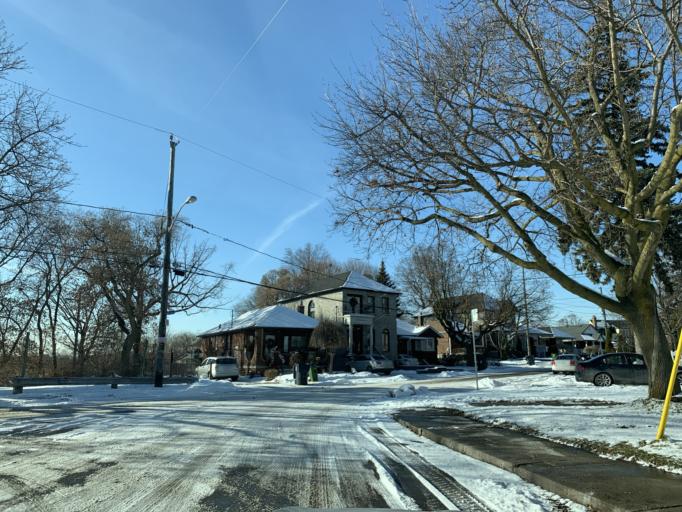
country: CA
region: Ontario
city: Toronto
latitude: 43.6854
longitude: -79.4769
